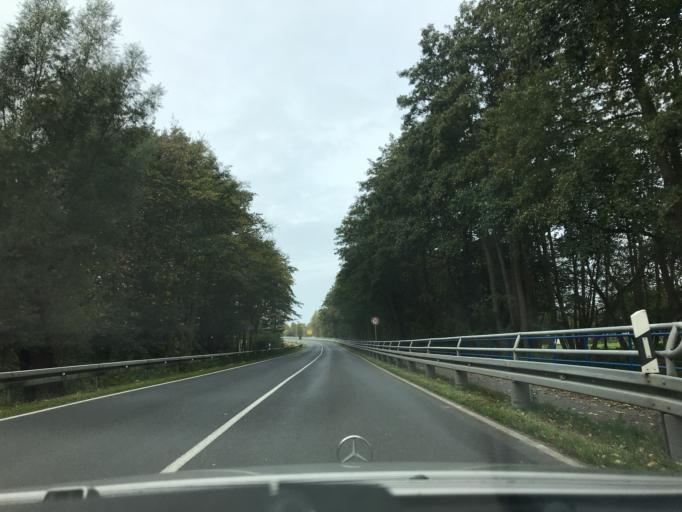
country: DE
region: Mecklenburg-Vorpommern
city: Lubmin
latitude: 54.1280
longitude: 13.6115
